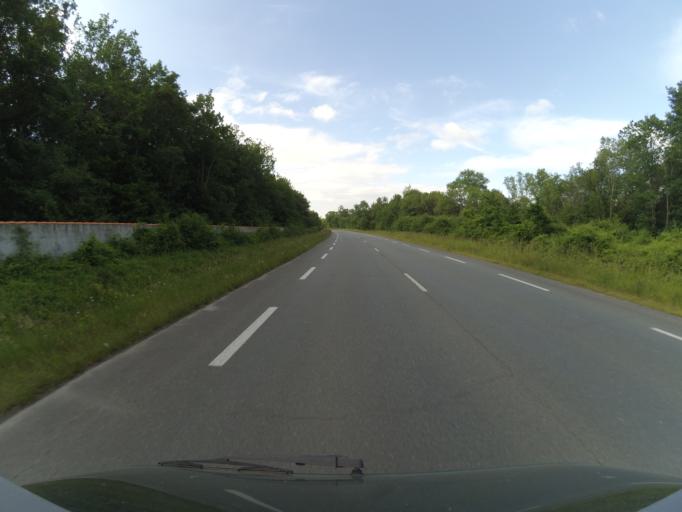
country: FR
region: Poitou-Charentes
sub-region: Departement de la Charente-Maritime
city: Saint-Agnant
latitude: 45.8137
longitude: -0.9314
